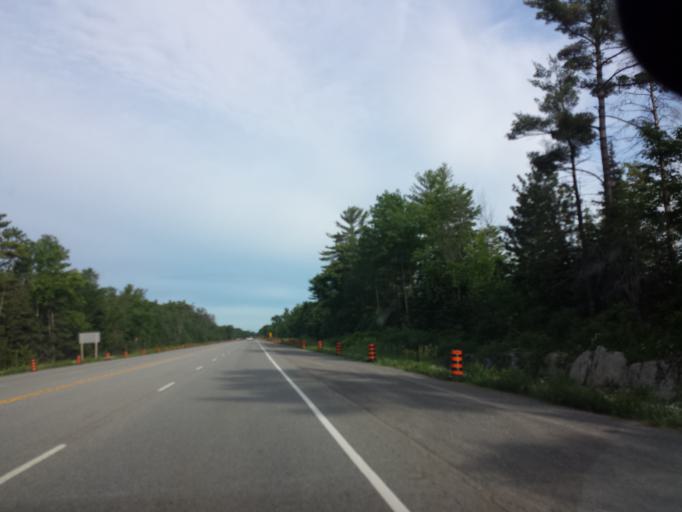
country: CA
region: Ontario
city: Arnprior
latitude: 45.4365
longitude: -76.4334
